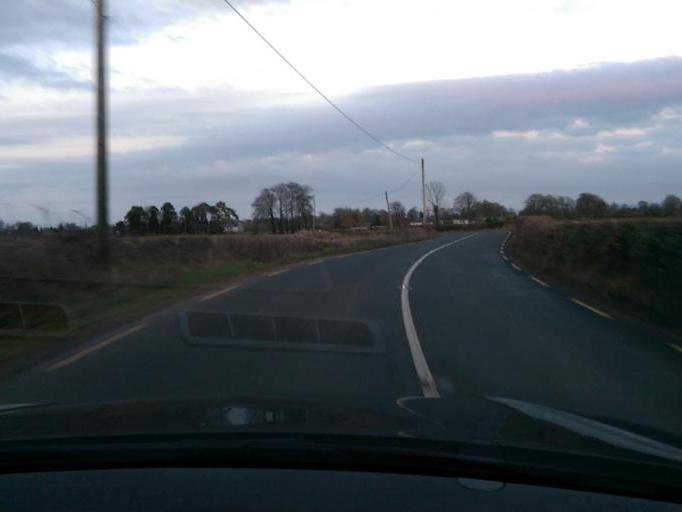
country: IE
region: Leinster
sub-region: Uibh Fhaili
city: Banagher
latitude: 53.0980
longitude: -8.0205
